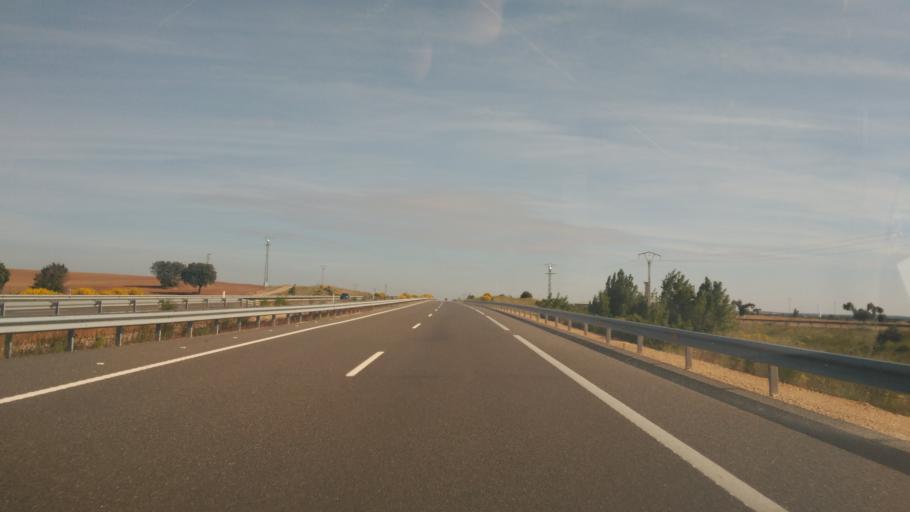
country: ES
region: Castille and Leon
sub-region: Provincia de Salamanca
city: Topas
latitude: 41.1848
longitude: -5.6959
